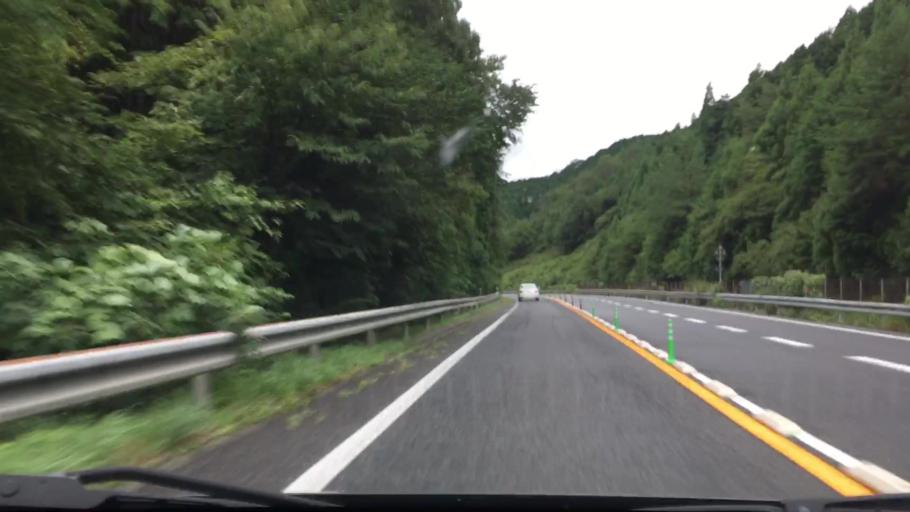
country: JP
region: Hyogo
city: Nishiwaki
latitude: 35.0965
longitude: 134.7763
